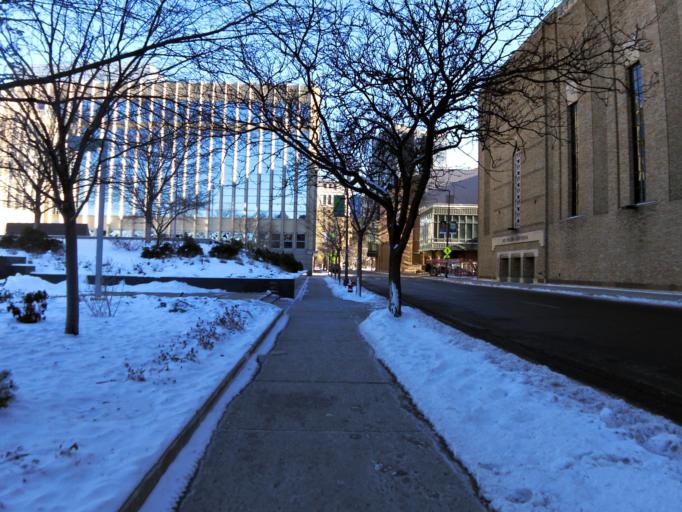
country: US
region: Minnesota
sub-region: Ramsey County
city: Saint Paul
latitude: 44.9455
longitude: -93.0996
